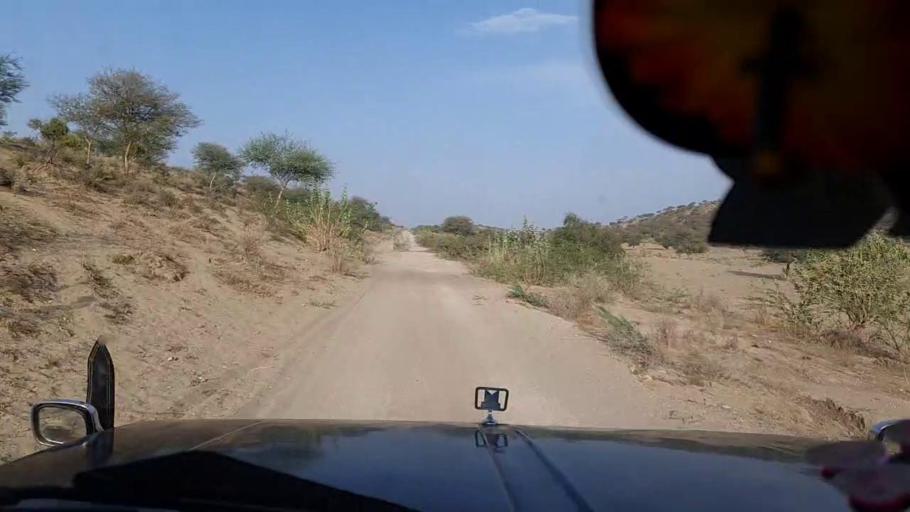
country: PK
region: Sindh
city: Diplo
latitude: 24.5521
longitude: 69.4615
